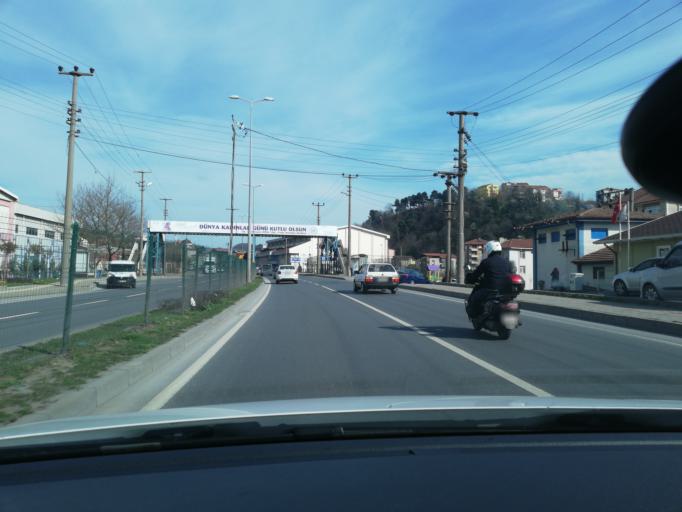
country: TR
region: Zonguldak
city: Eregli
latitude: 41.2692
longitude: 31.4399
